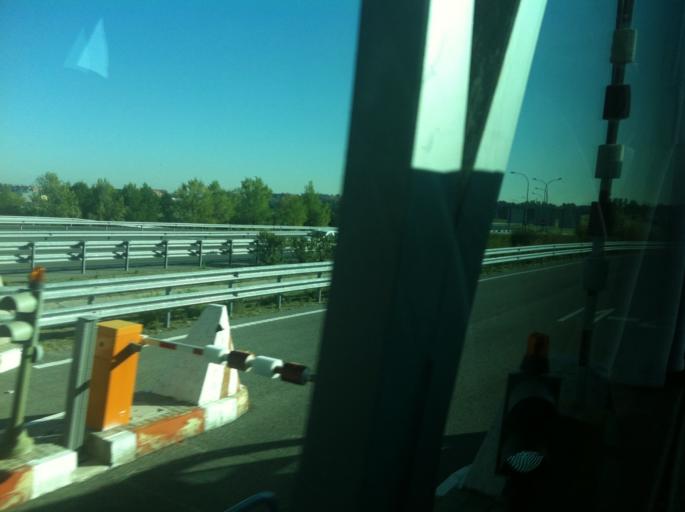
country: ES
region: Madrid
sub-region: Provincia de Madrid
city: Barajas de Madrid
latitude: 40.4743
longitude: -3.6016
